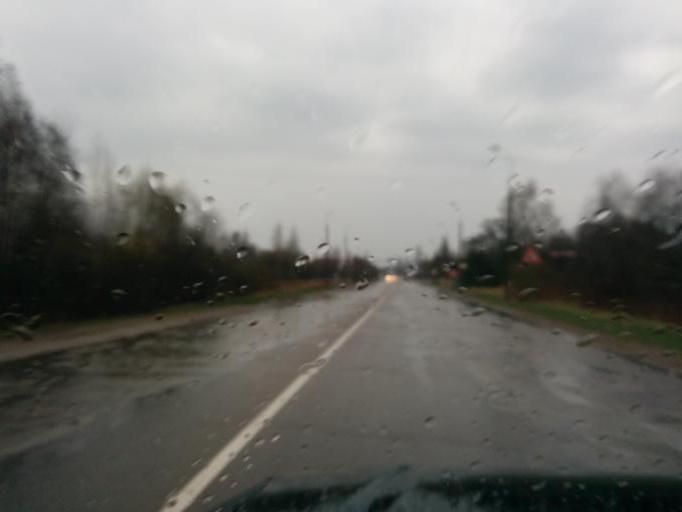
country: LV
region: Ozolnieku
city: Ozolnieki
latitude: 56.6591
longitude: 23.7882
